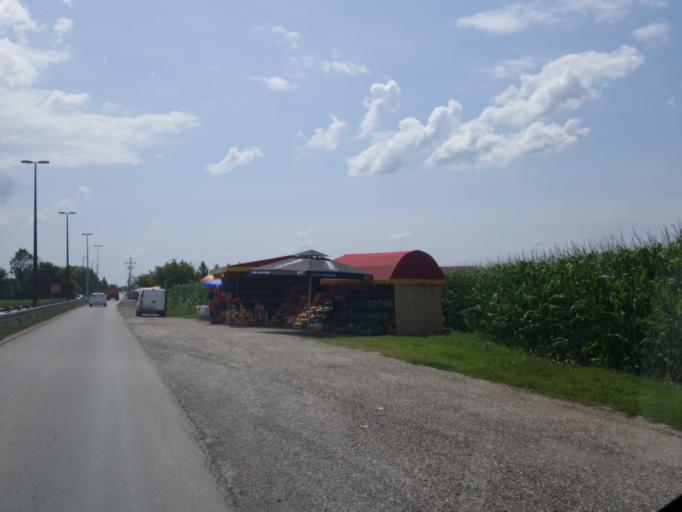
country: RS
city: Ravnje
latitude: 45.0343
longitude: 19.3860
